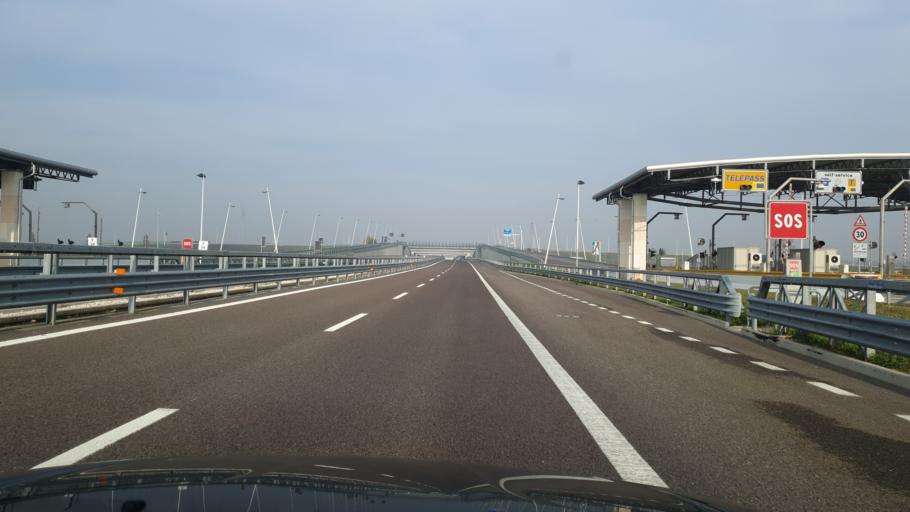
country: IT
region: Veneto
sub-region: Provincia di Vicenza
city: Noventa Vicentina
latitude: 45.2698
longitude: 11.5720
